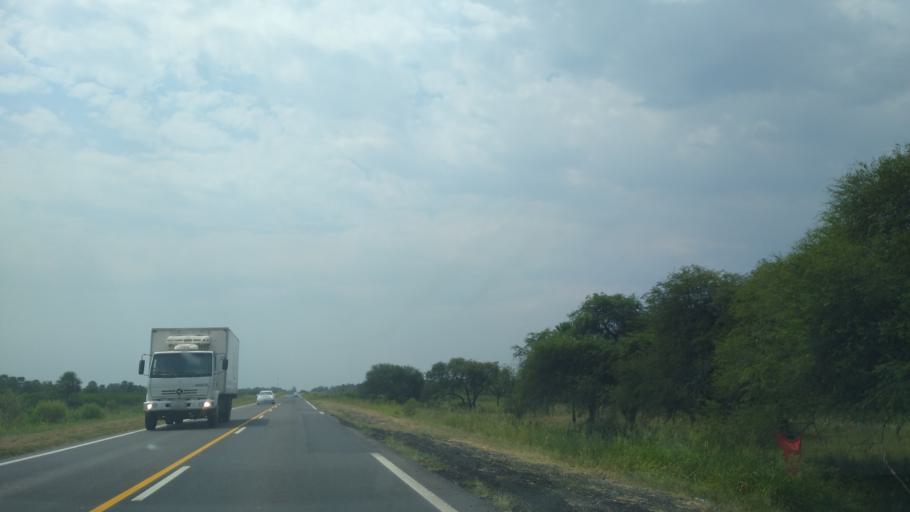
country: AR
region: Chaco
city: Margarita Belen
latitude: -27.1151
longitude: -58.9694
